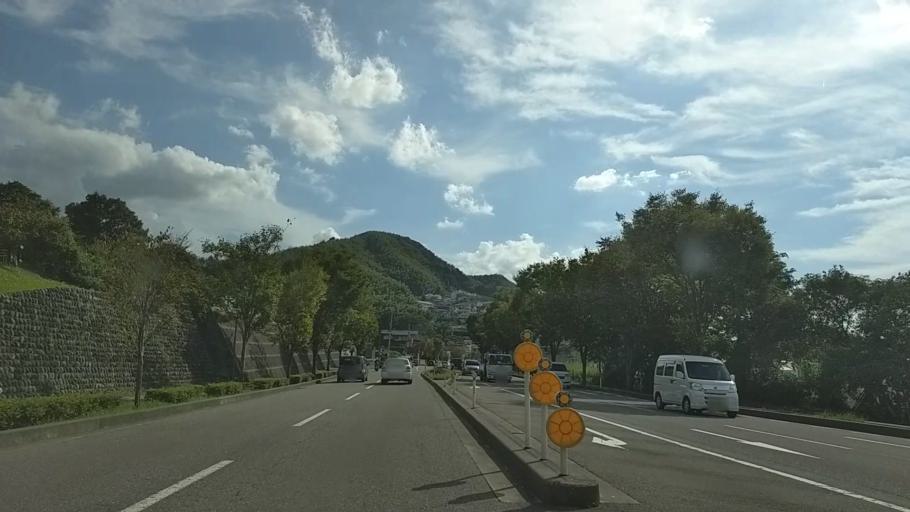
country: JP
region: Ishikawa
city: Nonoichi
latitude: 36.5303
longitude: 136.6525
